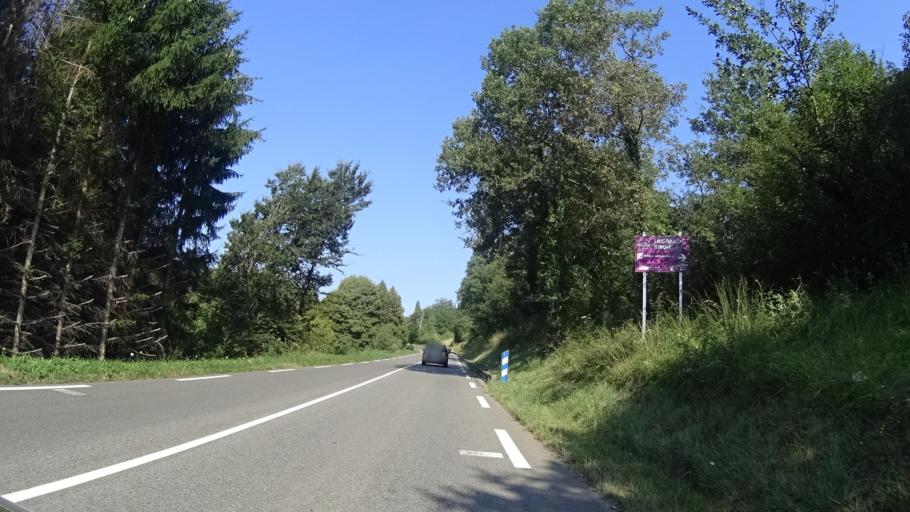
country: FR
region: Midi-Pyrenees
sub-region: Departement de l'Ariege
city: Lavelanet
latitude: 42.9220
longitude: 1.8801
